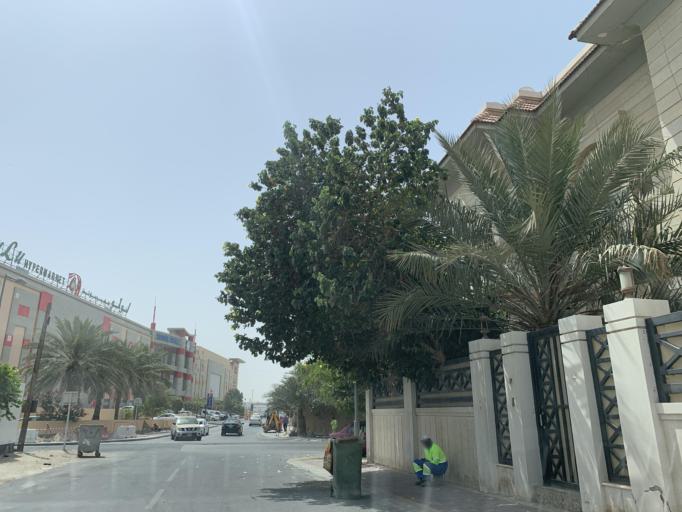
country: BH
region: Northern
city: Madinat `Isa
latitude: 26.1639
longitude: 50.5222
